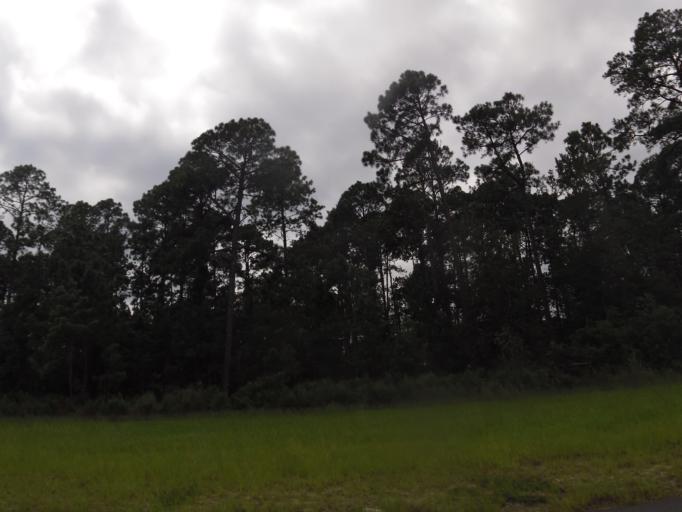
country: US
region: Georgia
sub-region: Glynn County
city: Brunswick
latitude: 31.1091
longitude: -81.5460
